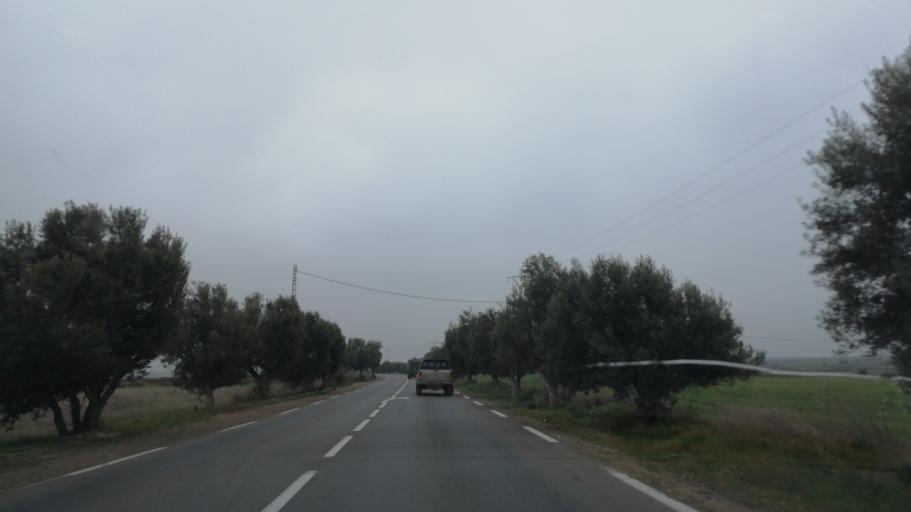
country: DZ
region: Mascara
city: Mascara
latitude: 35.3139
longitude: 0.3849
